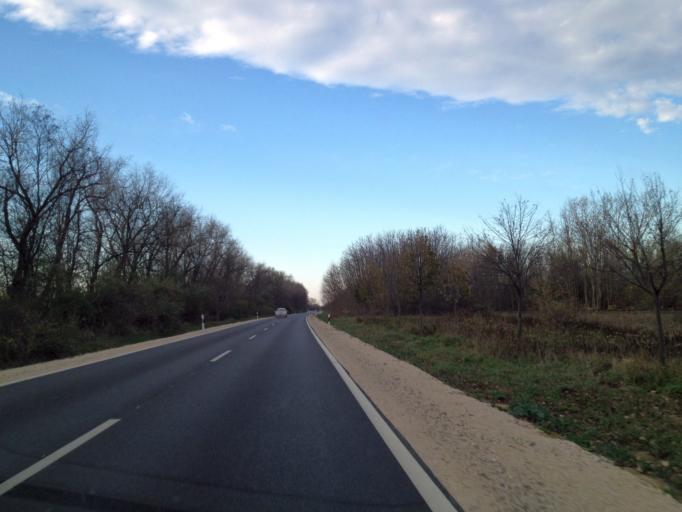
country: HU
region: Gyor-Moson-Sopron
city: Nyul
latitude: 47.6093
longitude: 17.6840
